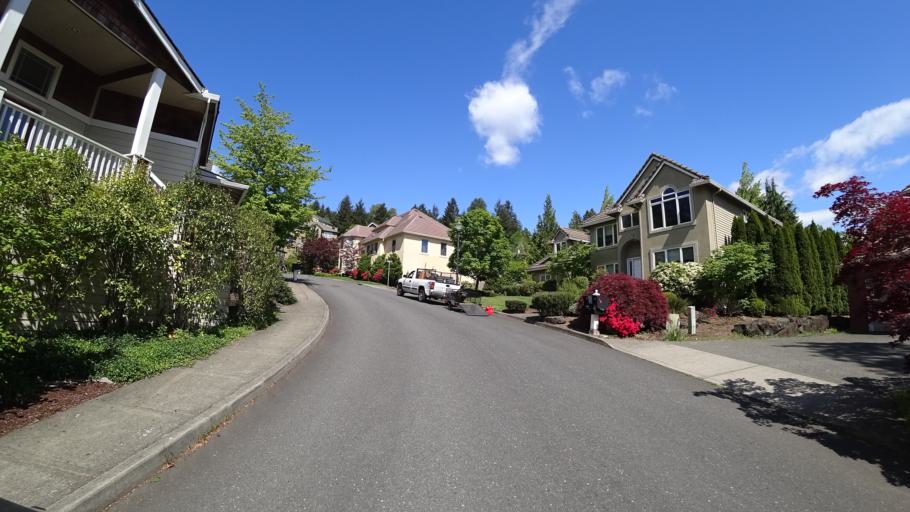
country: US
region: Oregon
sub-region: Washington County
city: West Haven
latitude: 45.5473
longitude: -122.7768
